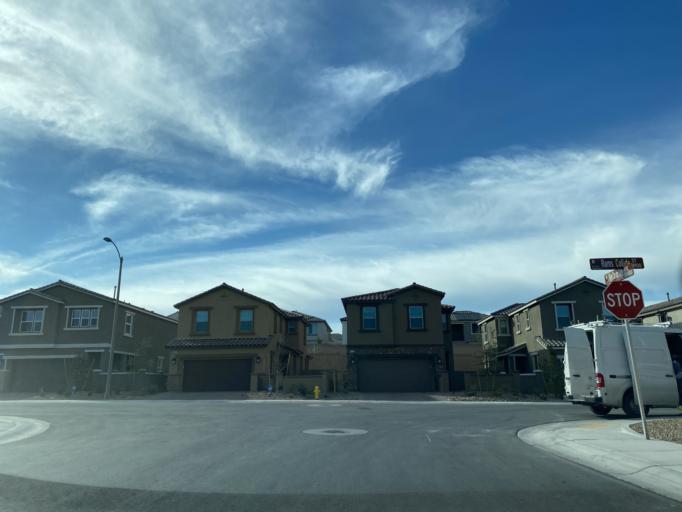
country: US
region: Nevada
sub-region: Clark County
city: Summerlin South
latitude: 36.3093
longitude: -115.3240
